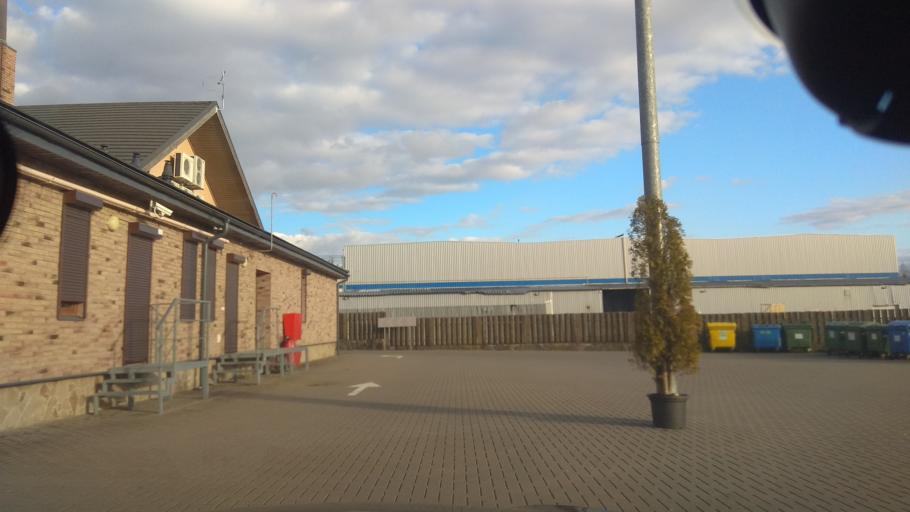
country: LT
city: Lentvaris
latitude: 54.7019
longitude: 25.0054
